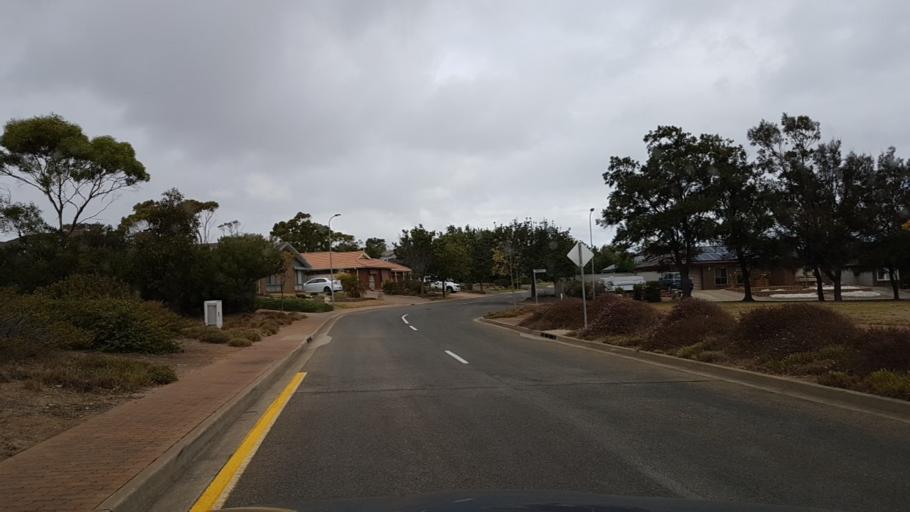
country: AU
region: South Australia
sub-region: Onkaparinga
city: Moana
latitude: -35.1968
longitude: 138.4898
